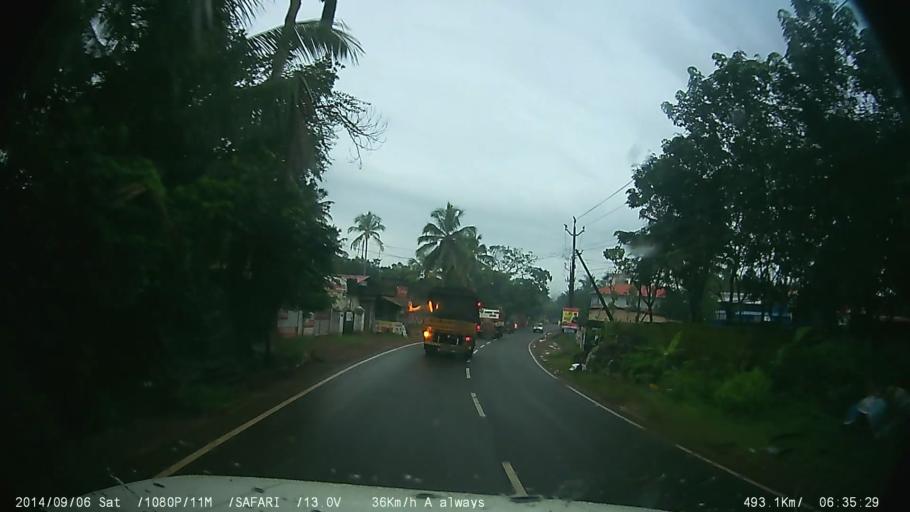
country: IN
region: Kerala
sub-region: Kottayam
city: Vaikam
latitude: 9.7866
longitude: 76.4555
